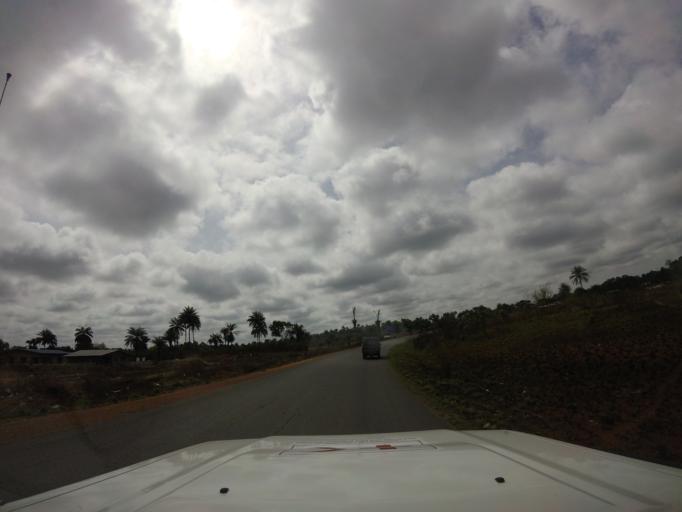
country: LR
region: Montserrado
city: Monrovia
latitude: 6.5135
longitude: -10.8222
